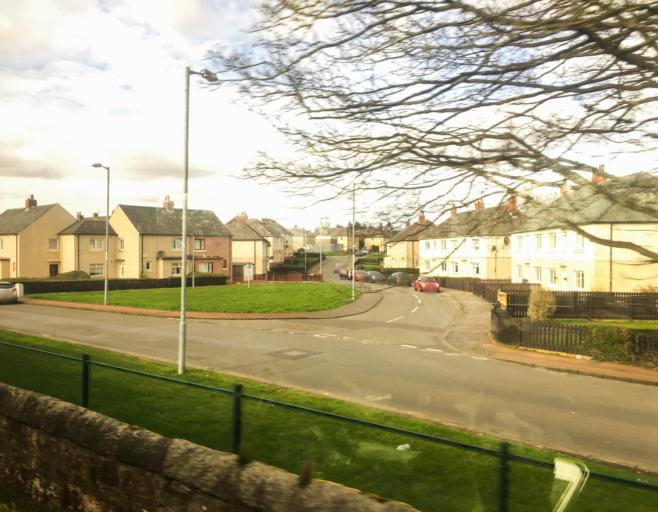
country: GB
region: Scotland
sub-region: North Lanarkshire
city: Wishaw
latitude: 55.7763
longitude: -3.9368
